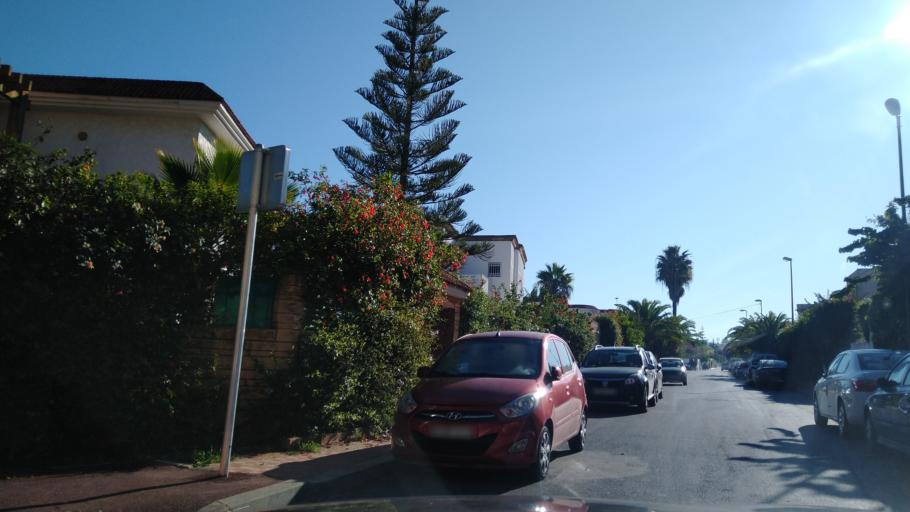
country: MA
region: Rabat-Sale-Zemmour-Zaer
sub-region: Skhirate-Temara
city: Temara
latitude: 33.9617
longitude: -6.8636
